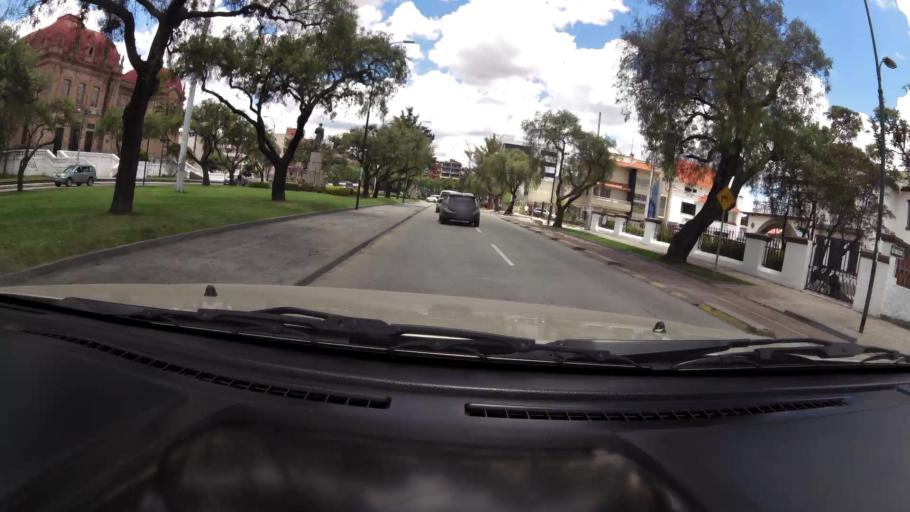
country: EC
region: Azuay
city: Cuenca
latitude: -2.9040
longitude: -79.0065
